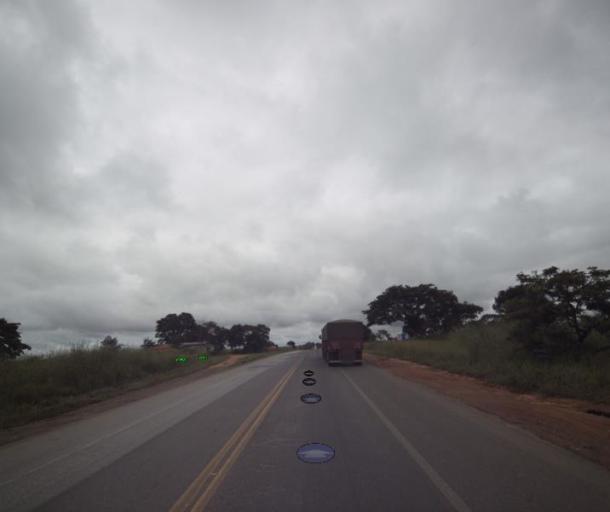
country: BR
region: Goias
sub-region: Uruacu
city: Uruacu
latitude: -14.6072
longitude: -49.1671
